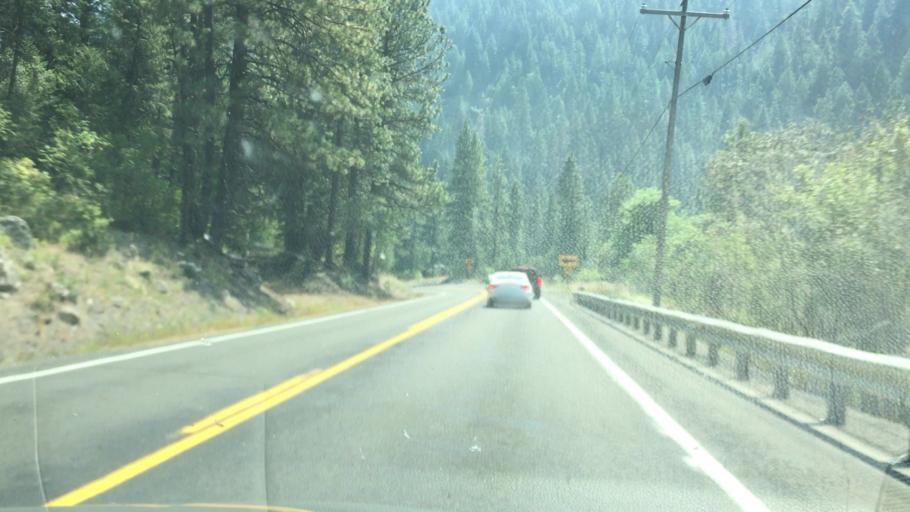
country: US
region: Idaho
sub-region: Valley County
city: McCall
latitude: 45.1507
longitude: -116.2966
